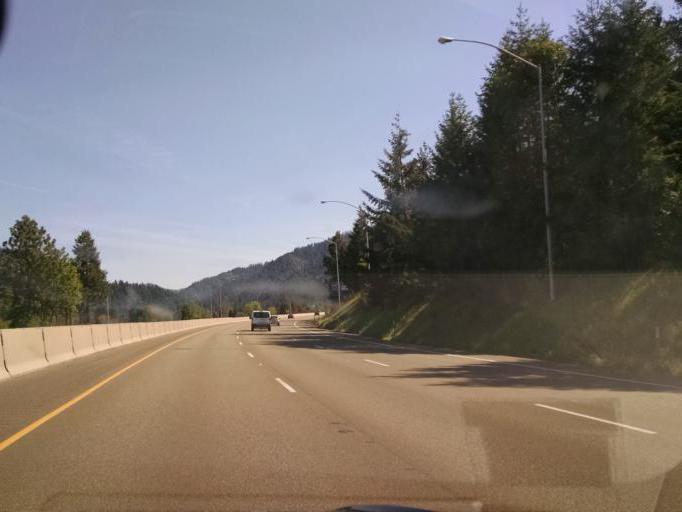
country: US
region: Oregon
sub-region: Douglas County
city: Canyonville
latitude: 42.9385
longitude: -123.2860
